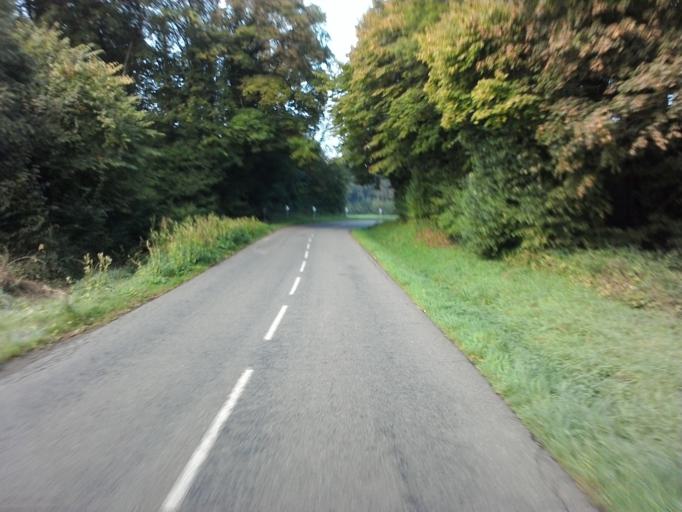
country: FR
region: Lorraine
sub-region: Departement de Meurthe-et-Moselle
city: Longuyon
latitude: 49.5087
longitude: 5.6116
